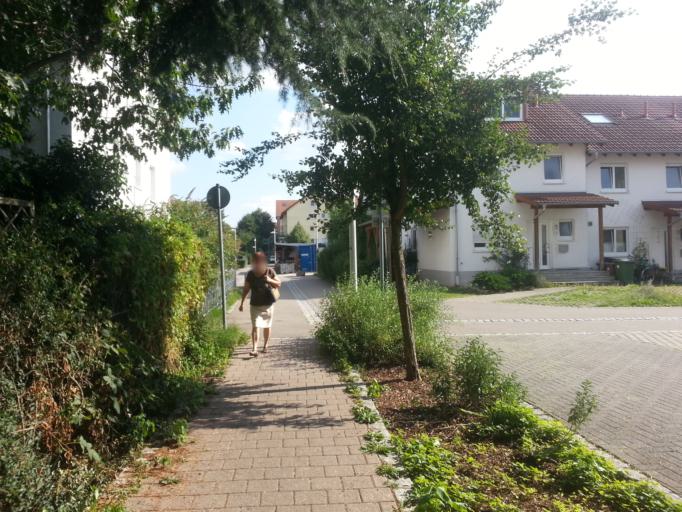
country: DE
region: Baden-Wuerttemberg
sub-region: Karlsruhe Region
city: Schriesheim
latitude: 49.4716
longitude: 8.6516
